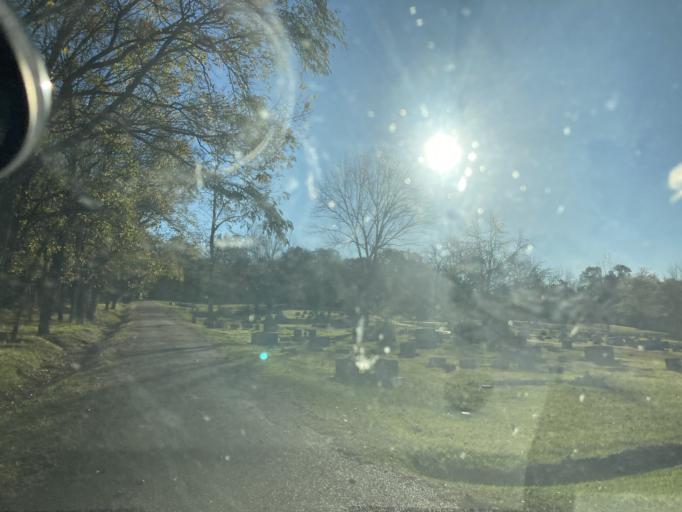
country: US
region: Mississippi
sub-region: Yazoo County
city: Yazoo City
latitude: 32.8515
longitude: -90.4005
